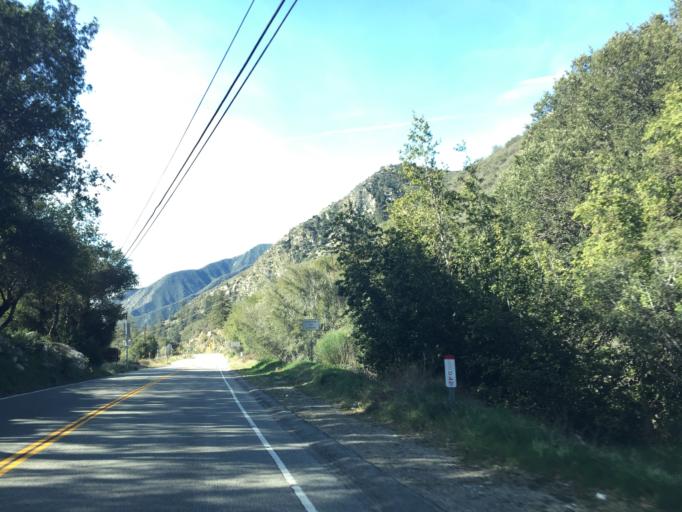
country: US
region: California
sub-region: San Bernardino County
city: San Antonio Heights
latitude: 34.2311
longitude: -117.6631
